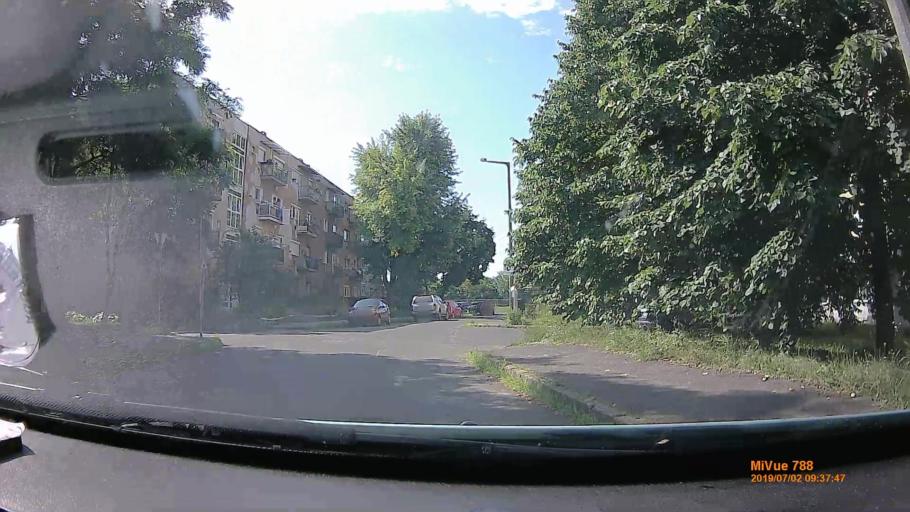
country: HU
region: Borsod-Abauj-Zemplen
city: Miskolc
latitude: 48.1012
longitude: 20.8033
